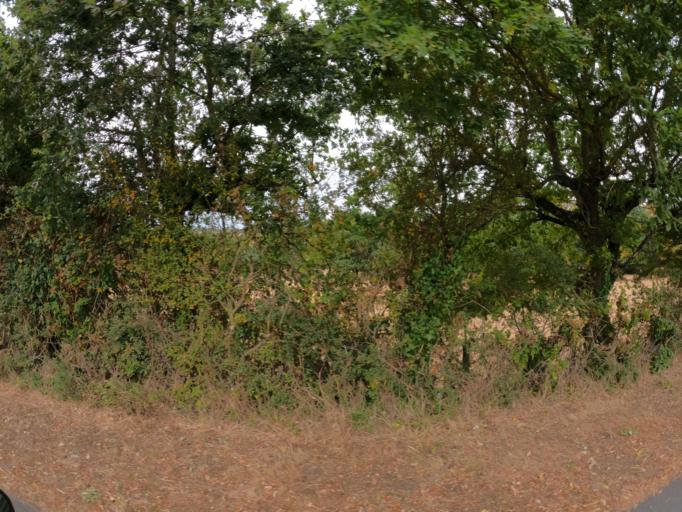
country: FR
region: Pays de la Loire
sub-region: Departement de la Vendee
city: Tiffauges
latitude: 47.0106
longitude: -1.1155
